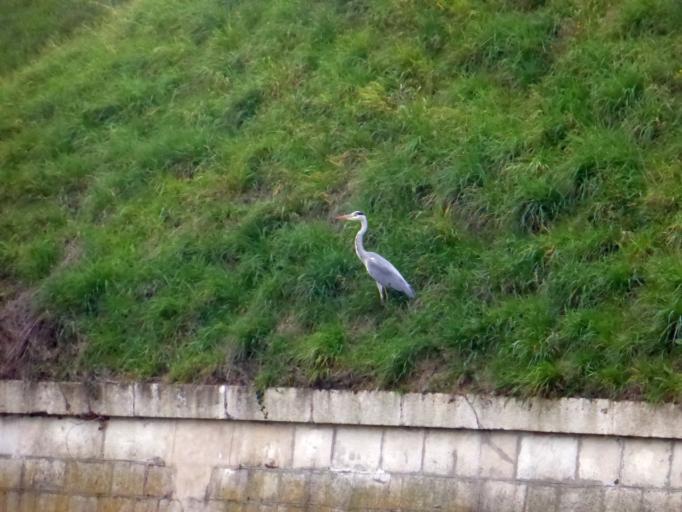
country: FR
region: Lorraine
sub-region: Departement de Meurthe-et-Moselle
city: Toul
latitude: 48.6766
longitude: 5.8854
